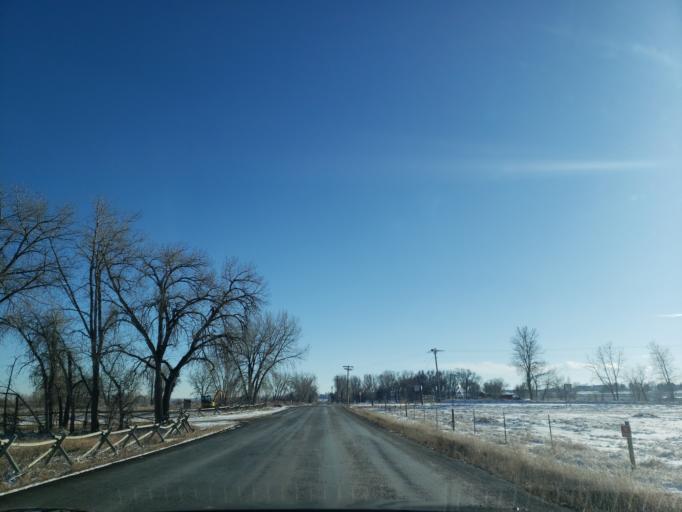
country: US
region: Colorado
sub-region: Larimer County
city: Fort Collins
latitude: 40.5324
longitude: -105.0013
